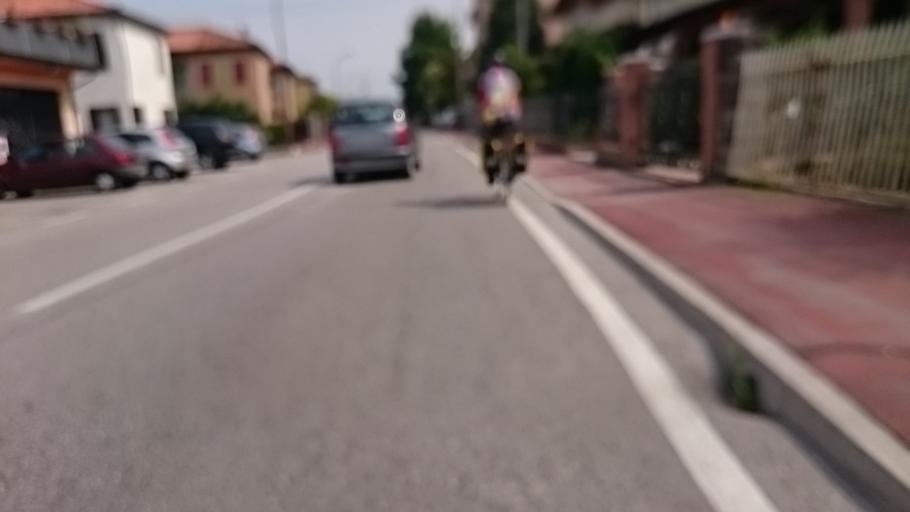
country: IT
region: Veneto
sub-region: Provincia di Venezia
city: Fornase
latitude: 45.4573
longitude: 12.1738
